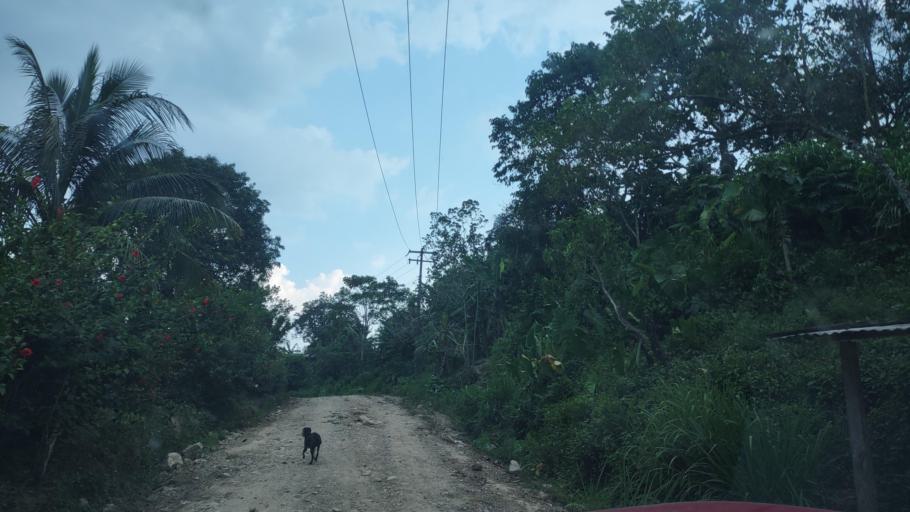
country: MX
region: Chiapas
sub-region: Tecpatan
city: Raudales Malpaso
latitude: 17.3103
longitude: -93.7783
